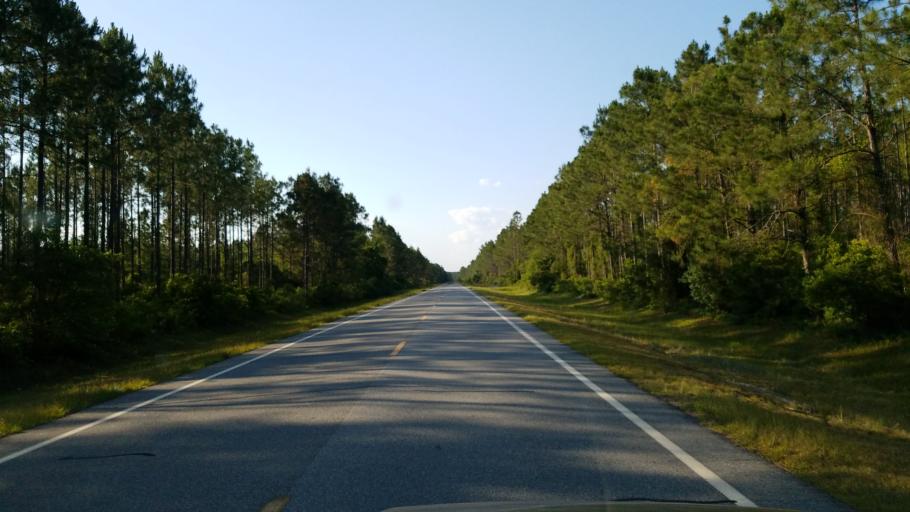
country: US
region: Georgia
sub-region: Lanier County
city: Lakeland
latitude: 30.8723
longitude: -83.0523
